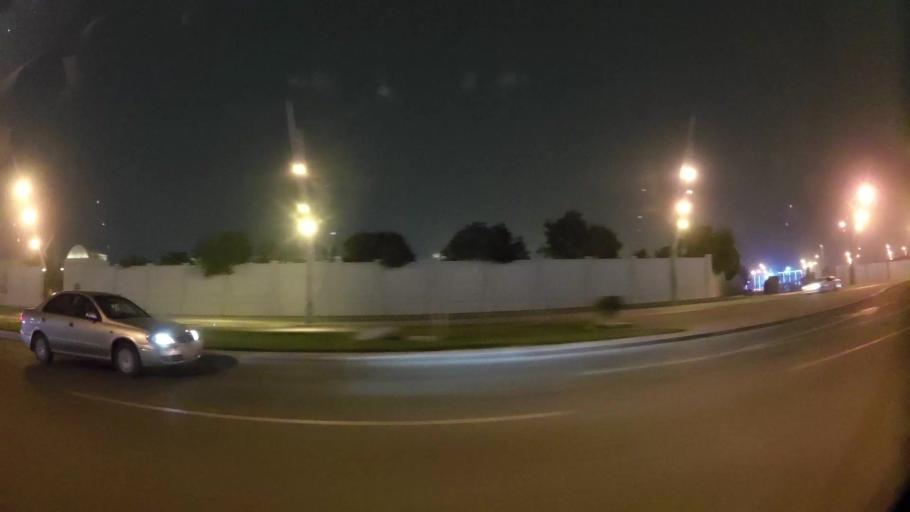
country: QA
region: Baladiyat ar Rayyan
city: Ar Rayyan
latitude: 25.2621
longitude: 51.4536
